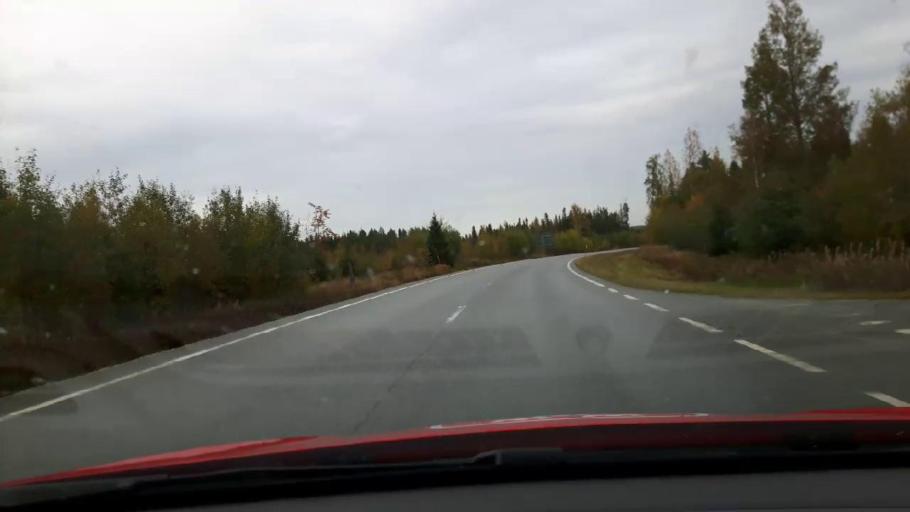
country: SE
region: Jaemtland
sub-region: Bergs Kommun
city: Hoverberg
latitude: 62.9154
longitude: 14.3283
